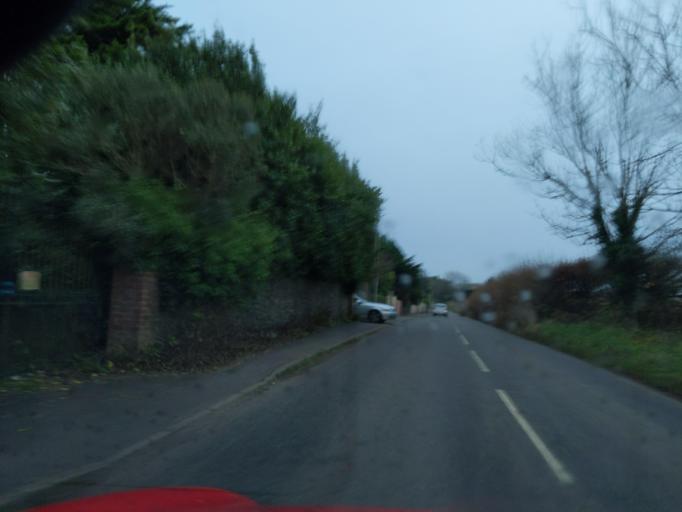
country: GB
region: England
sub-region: Devon
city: Wembury
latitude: 50.3394
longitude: -4.0736
